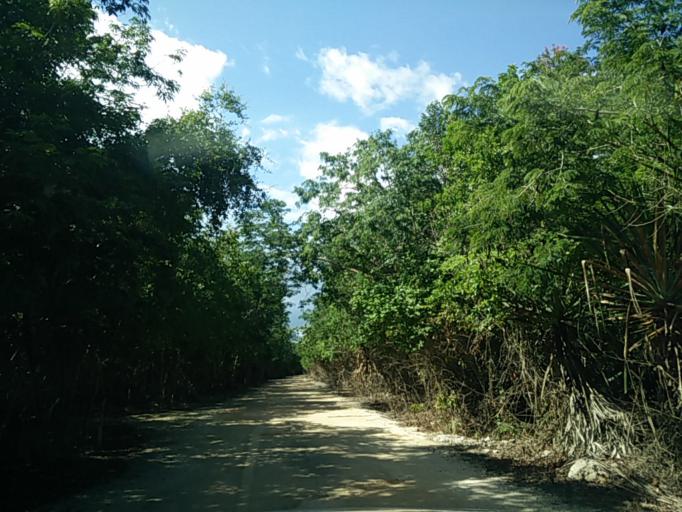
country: MX
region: Quintana Roo
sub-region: Tulum
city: Ciudad Chemuyil
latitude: 20.4970
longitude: -87.2577
